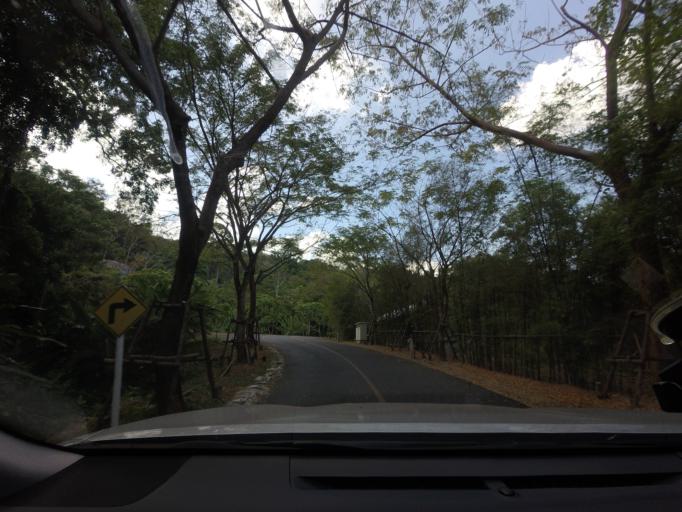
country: TH
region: Phuket
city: Mueang Phuket
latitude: 7.8756
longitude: 98.3528
